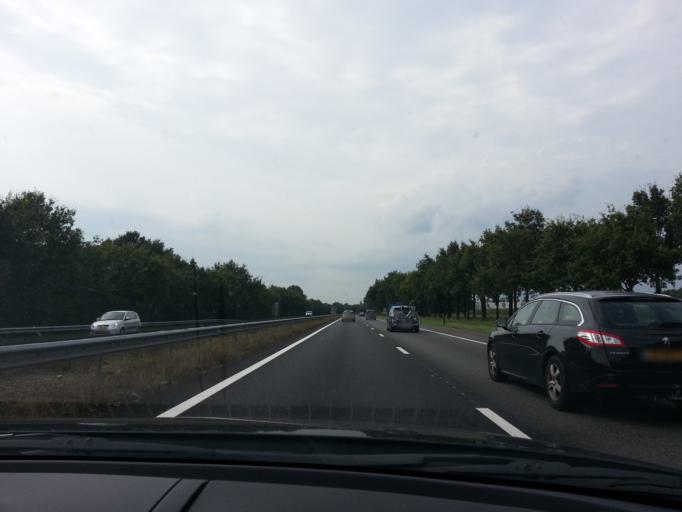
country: NL
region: North Brabant
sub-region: Gemeente Cranendonck
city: Cranendonck
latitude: 51.3011
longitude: 5.6208
